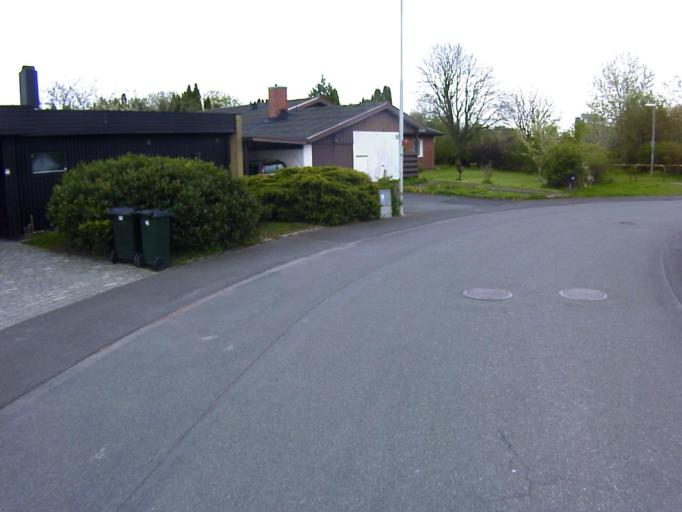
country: SE
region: Skane
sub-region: Kristianstads Kommun
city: Kristianstad
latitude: 56.0472
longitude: 14.1798
